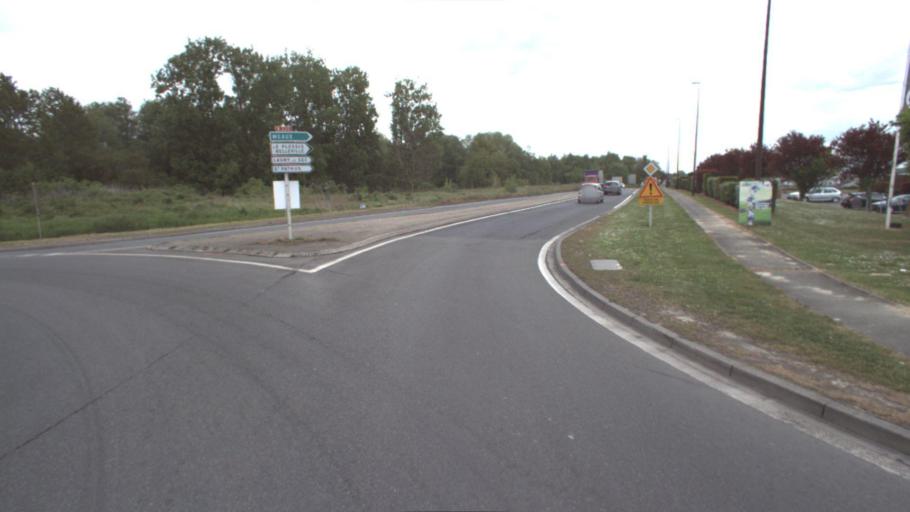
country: FR
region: Picardie
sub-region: Departement de l'Oise
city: Lagny-le-Sec
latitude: 49.0975
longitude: 2.7397
